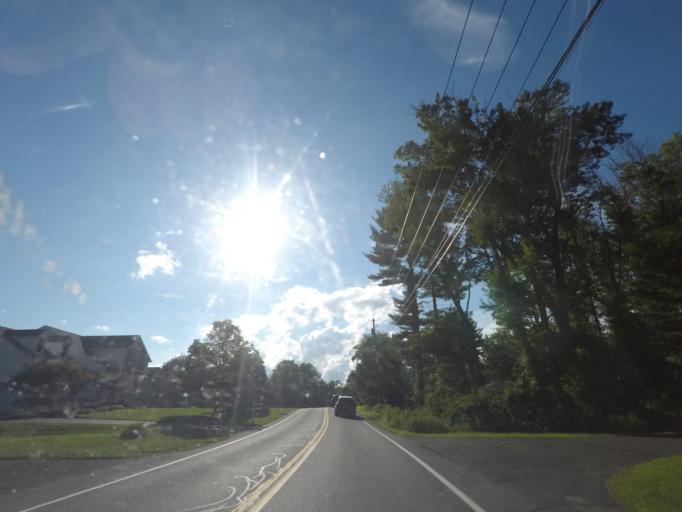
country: US
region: New York
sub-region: Albany County
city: Roessleville
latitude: 42.7279
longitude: -73.7827
